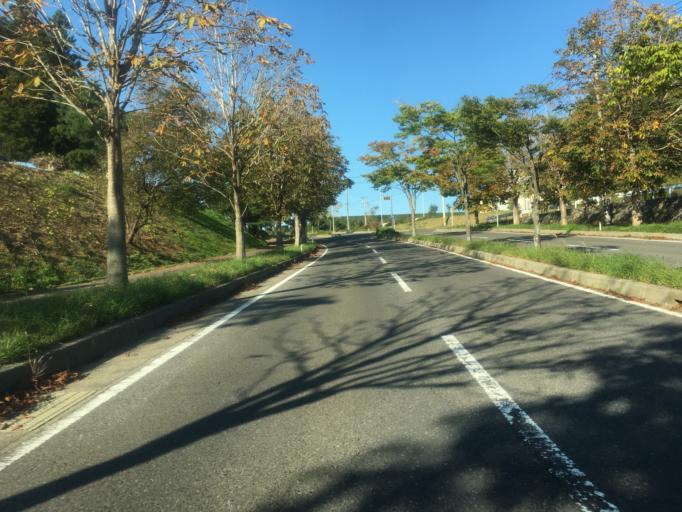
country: JP
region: Fukushima
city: Fukushima-shi
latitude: 37.6864
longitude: 140.4757
